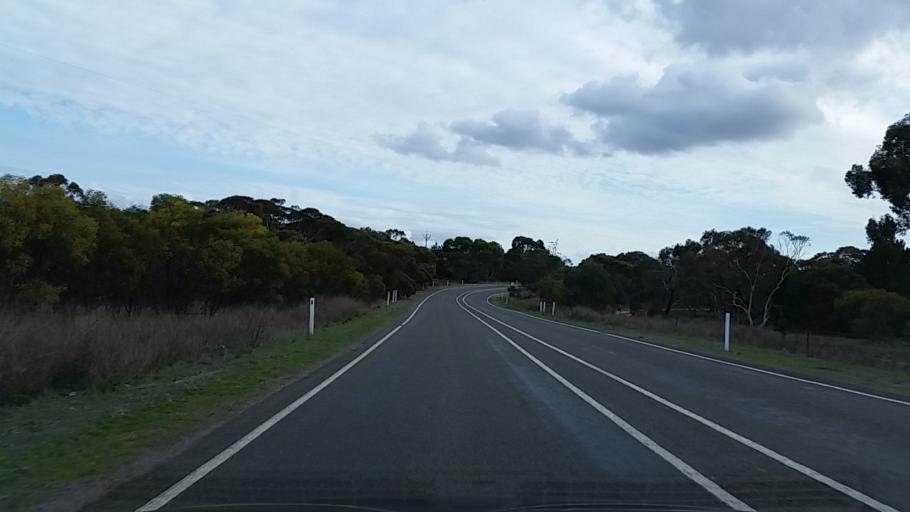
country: AU
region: South Australia
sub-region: Mount Barker
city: Callington
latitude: -35.1179
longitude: 139.1495
